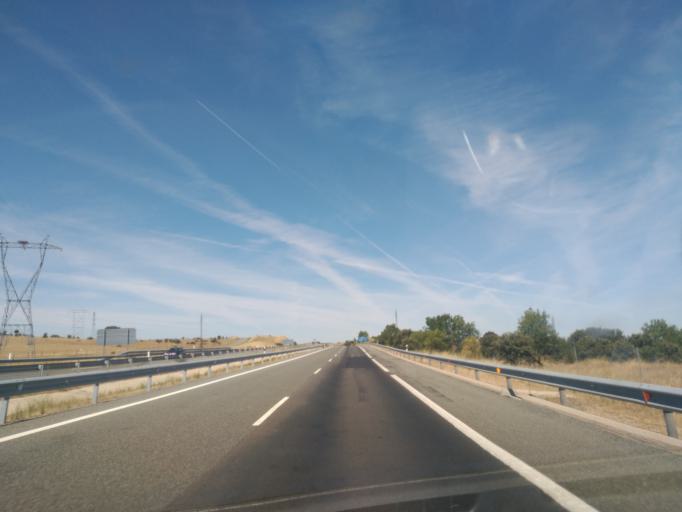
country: ES
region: Castille and Leon
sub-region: Provincia de Salamanca
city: Guijuelo
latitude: 40.5304
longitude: -5.6684
